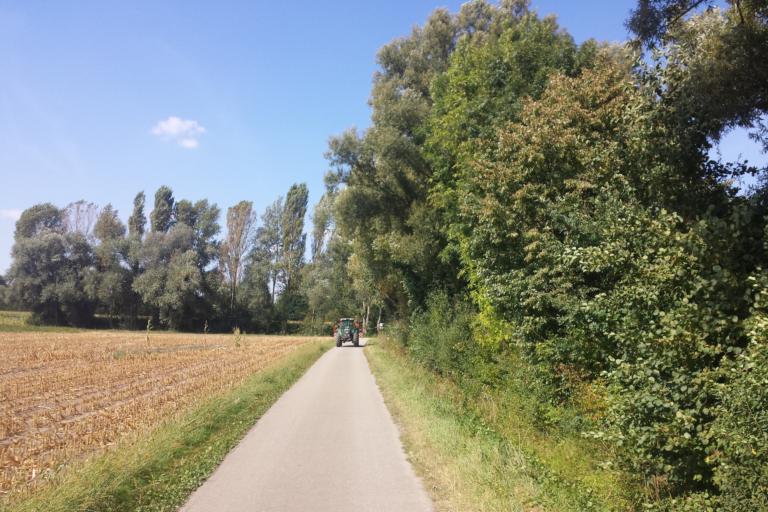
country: DE
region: Hesse
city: Lorsch
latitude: 49.6259
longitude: 8.5825
